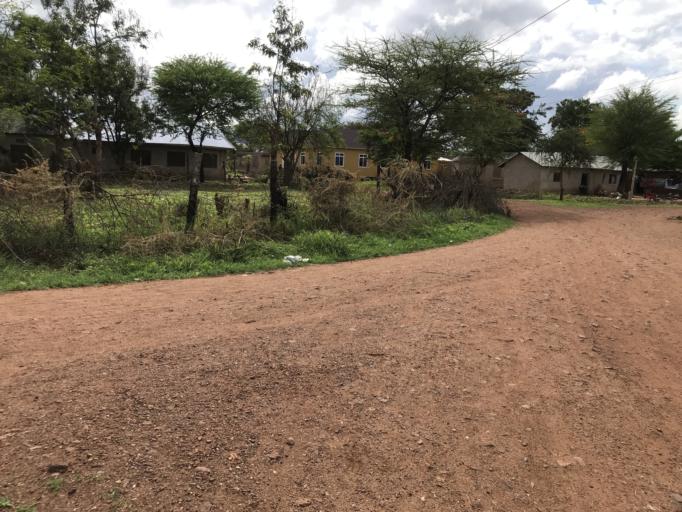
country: TZ
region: Tabora
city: Igunga
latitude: -4.2889
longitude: 33.8828
